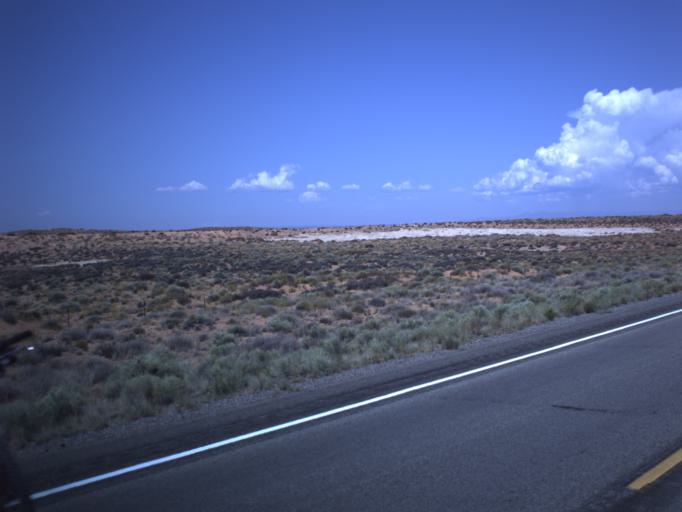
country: US
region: Utah
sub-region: San Juan County
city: Blanding
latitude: 37.0817
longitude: -109.5480
